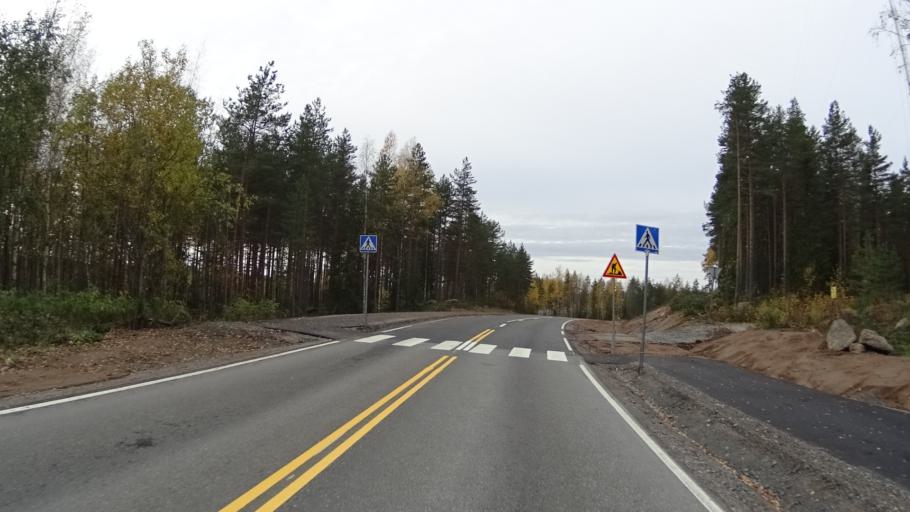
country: FI
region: South Karelia
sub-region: Lappeenranta
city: Luumaeki
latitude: 60.9376
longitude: 27.6764
